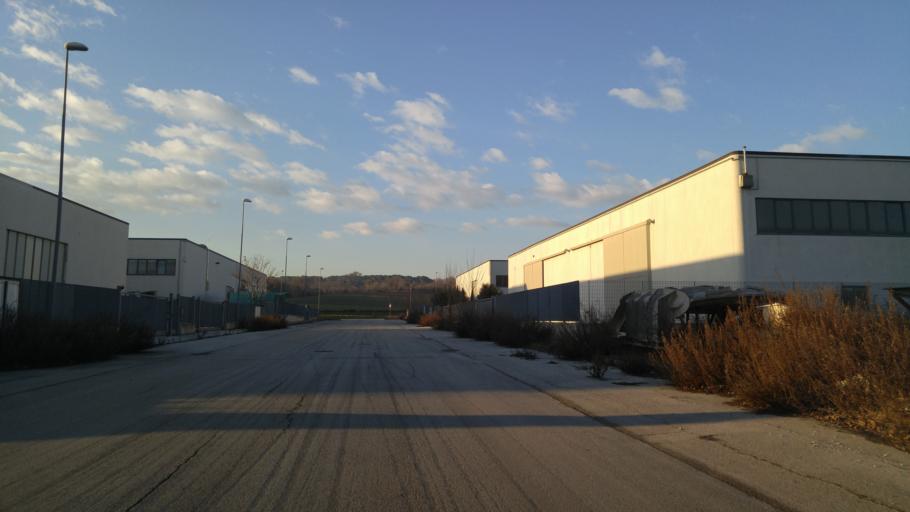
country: IT
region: The Marches
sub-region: Provincia di Ancona
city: Monterado
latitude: 43.7117
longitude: 13.0795
